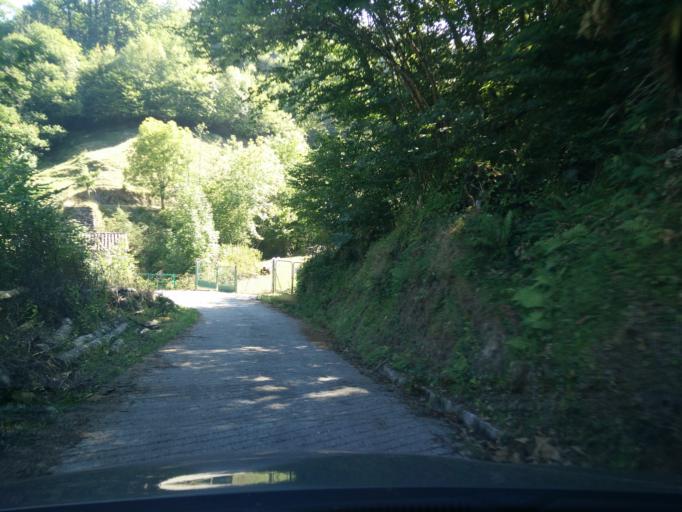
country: ES
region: Asturias
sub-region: Province of Asturias
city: Campo de Caso
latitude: 43.1501
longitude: -5.3798
